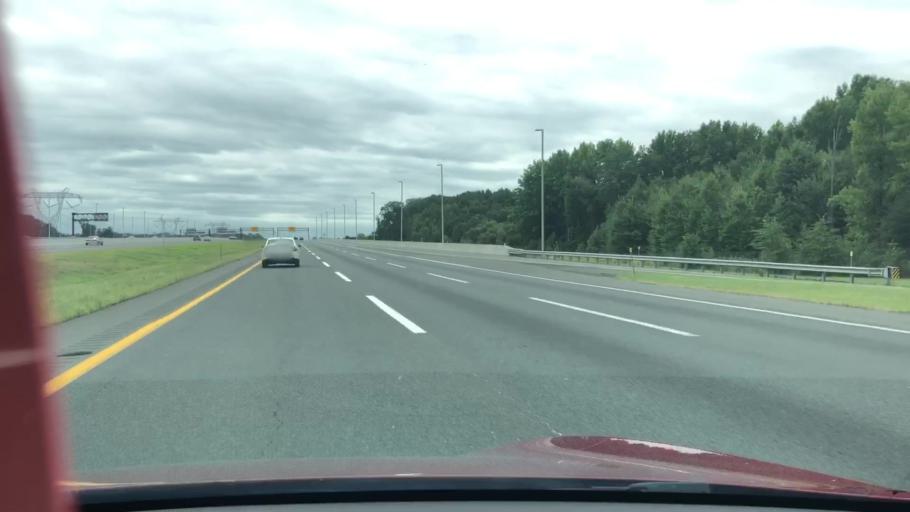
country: US
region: New Jersey
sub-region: Burlington County
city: Roebling
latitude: 40.0939
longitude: -74.7340
